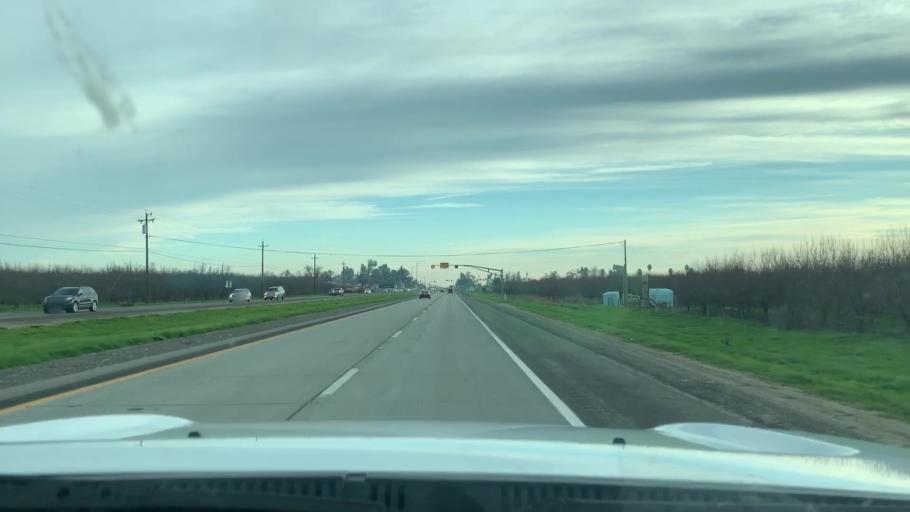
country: US
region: California
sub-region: Kings County
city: Lemoore
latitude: 36.3471
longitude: -119.8083
